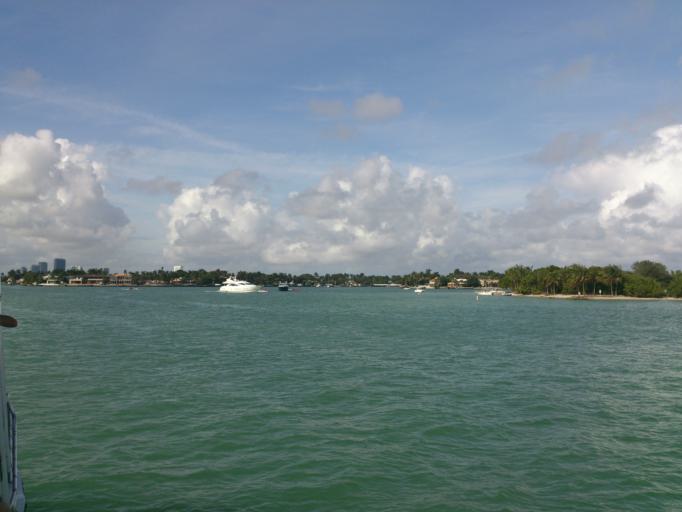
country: US
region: Florida
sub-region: Miami-Dade County
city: Miami Beach
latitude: 25.7826
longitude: -80.1524
